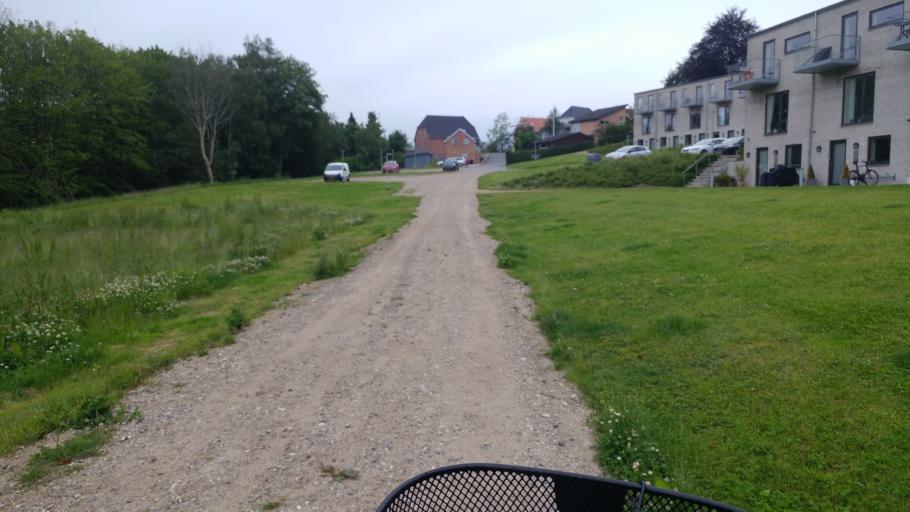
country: DK
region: Central Jutland
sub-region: Skanderborg Kommune
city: Horning
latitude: 56.0841
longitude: 10.0407
